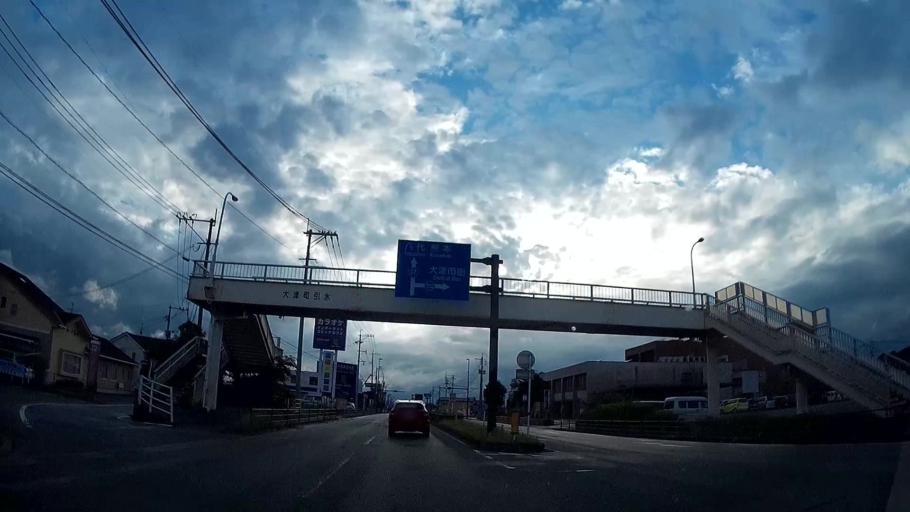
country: JP
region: Kumamoto
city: Ozu
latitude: 32.8755
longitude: 130.8767
